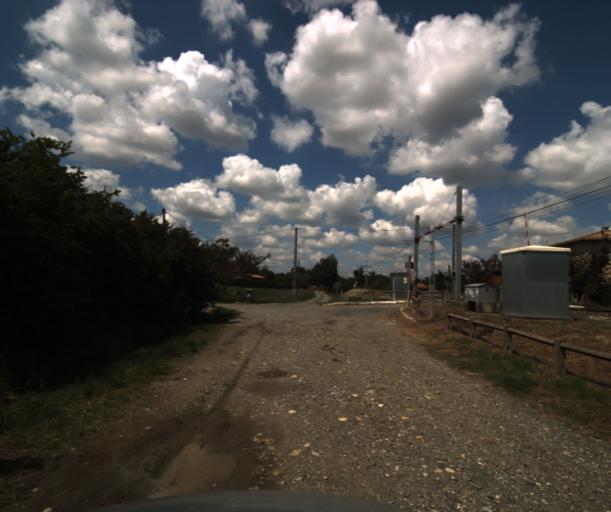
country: FR
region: Midi-Pyrenees
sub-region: Departement de la Haute-Garonne
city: Pinsaguel
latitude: 43.4952
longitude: 1.3925
